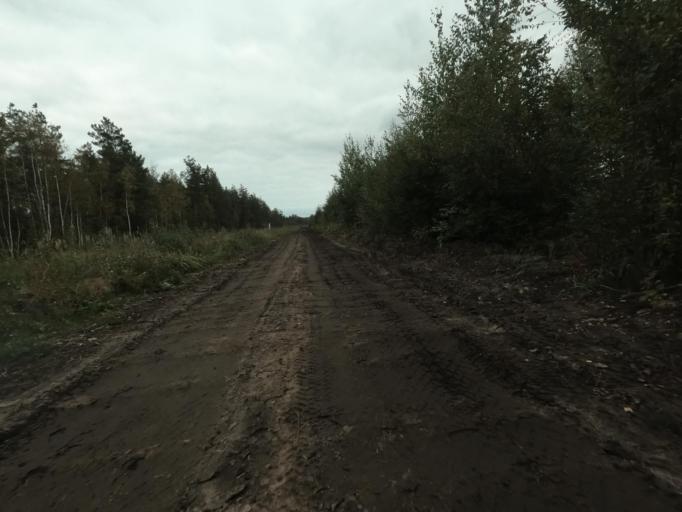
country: RU
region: St.-Petersburg
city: Sapernyy
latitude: 59.7624
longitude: 30.7208
